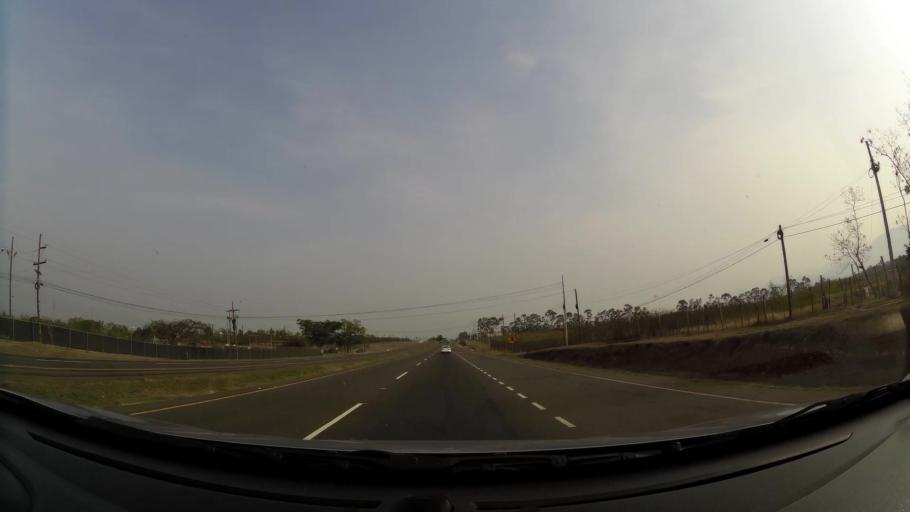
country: HN
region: La Paz
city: Yarumela
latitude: 14.3876
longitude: -87.6126
